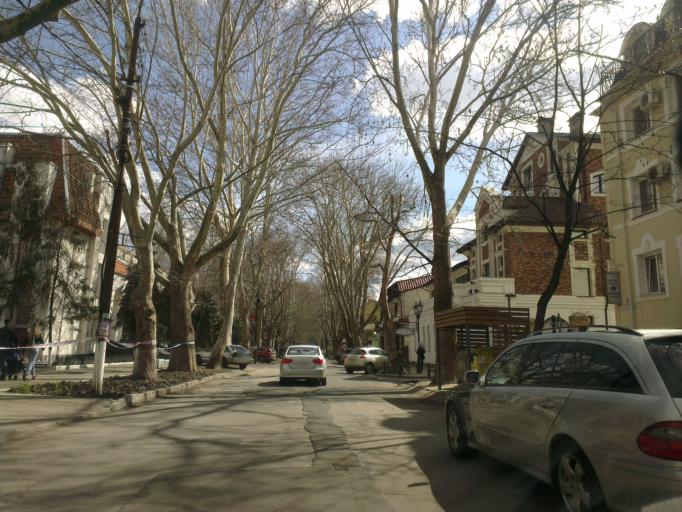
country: MD
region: Chisinau
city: Chisinau
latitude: 47.0208
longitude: 28.8322
